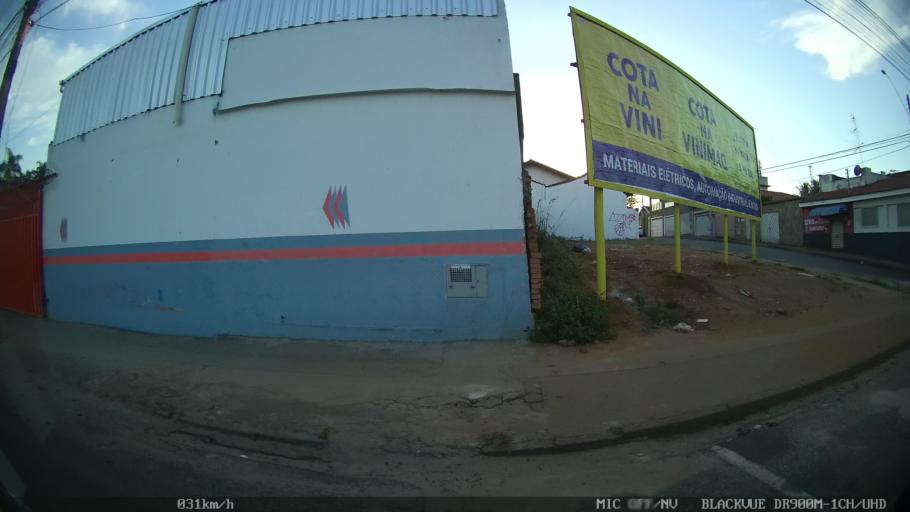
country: BR
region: Sao Paulo
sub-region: Franca
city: Franca
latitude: -20.5219
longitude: -47.4068
